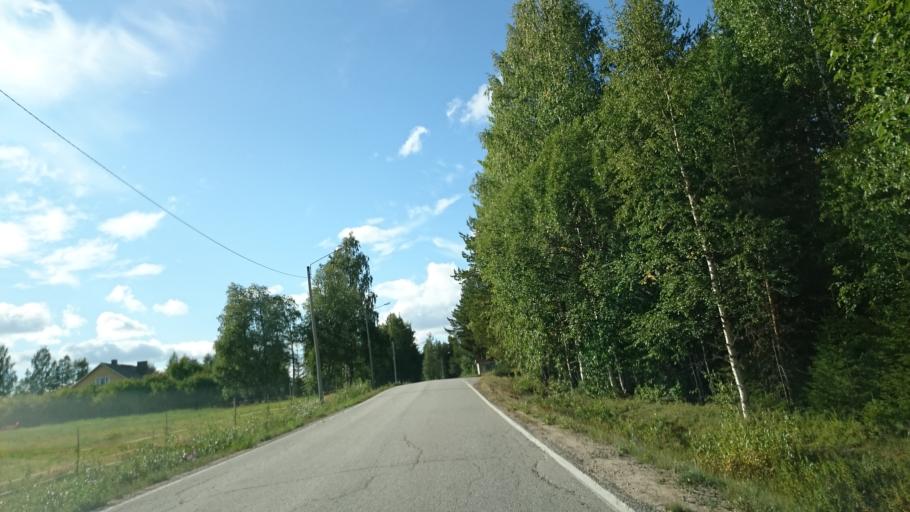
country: FI
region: Kainuu
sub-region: Kehys-Kainuu
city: Suomussalmi
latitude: 64.7463
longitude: 29.4452
